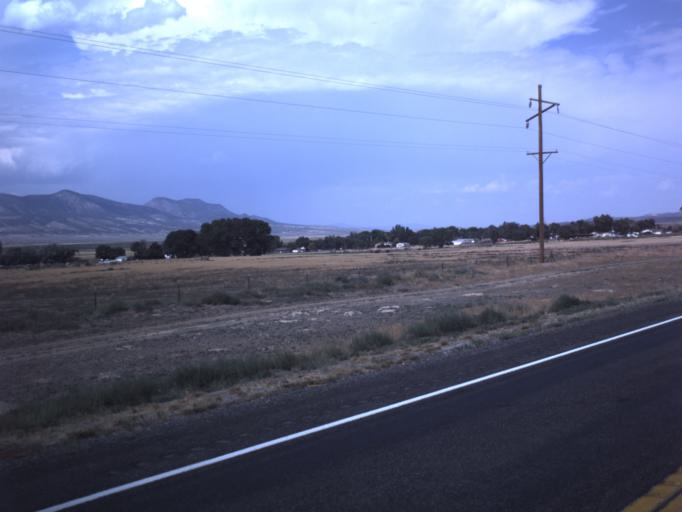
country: US
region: Utah
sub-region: Sanpete County
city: Gunnison
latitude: 39.2156
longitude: -111.8483
